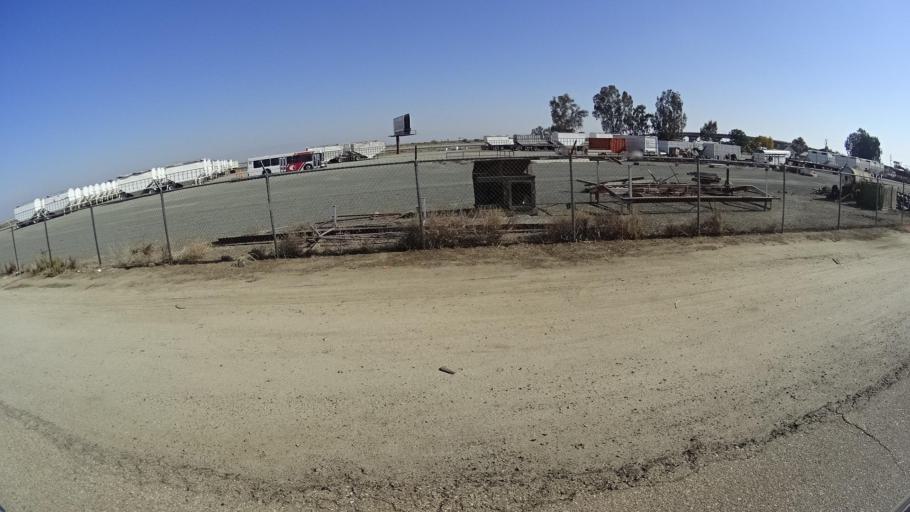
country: US
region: California
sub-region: Kern County
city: McFarland
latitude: 35.6909
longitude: -119.2320
